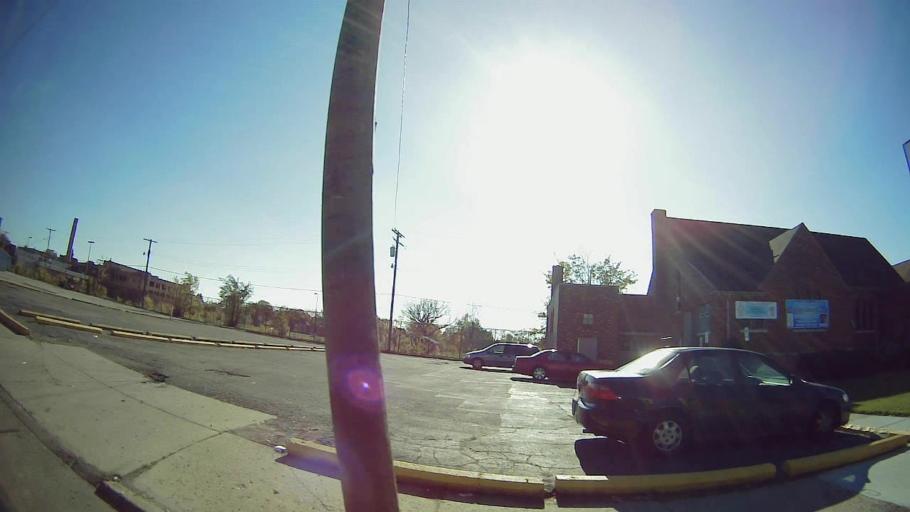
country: US
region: Michigan
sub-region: Oakland County
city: Oak Park
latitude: 42.4016
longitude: -83.1929
